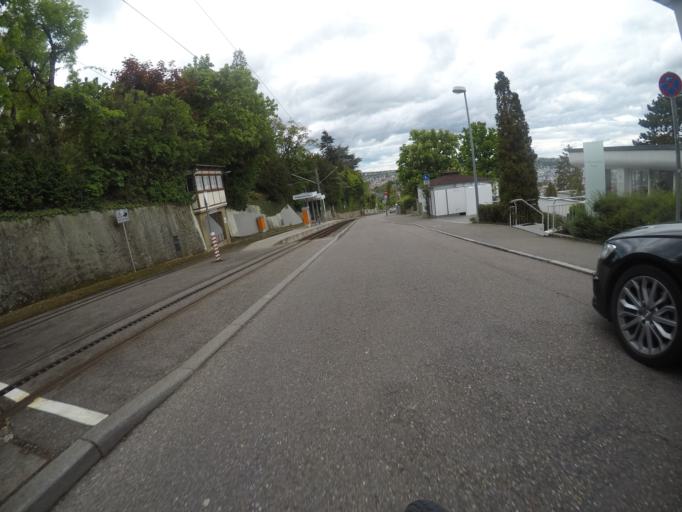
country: DE
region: Baden-Wuerttemberg
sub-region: Regierungsbezirk Stuttgart
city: Stuttgart
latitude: 48.7571
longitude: 9.1705
